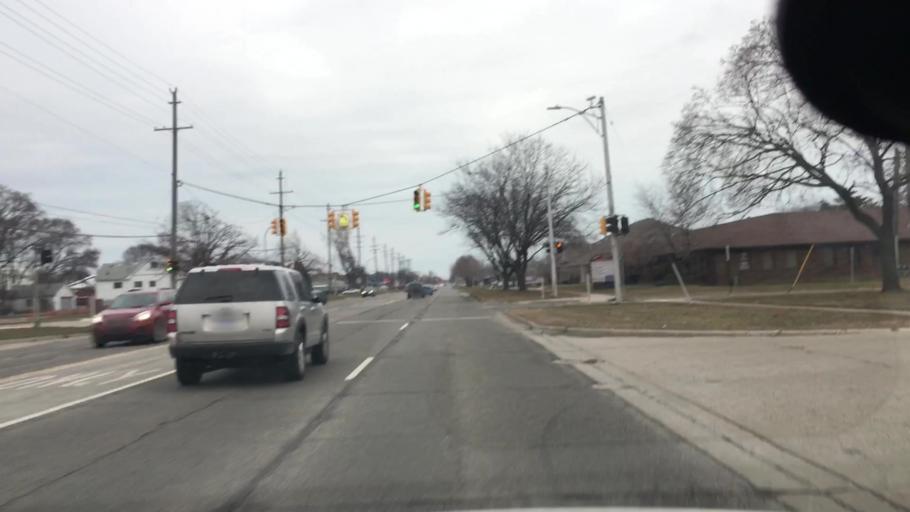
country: US
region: Michigan
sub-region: Oakland County
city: Madison Heights
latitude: 42.5055
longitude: -83.0745
